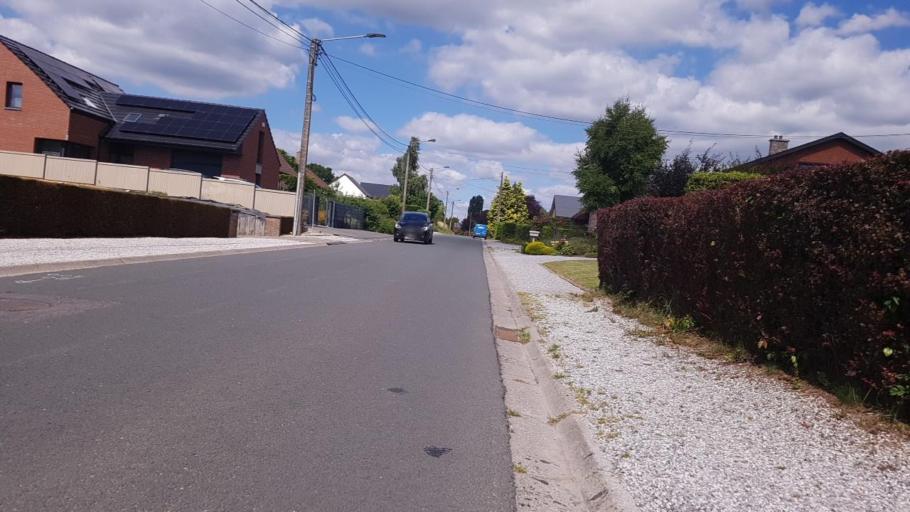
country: BE
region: Wallonia
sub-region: Province de Namur
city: Walcourt
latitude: 50.3342
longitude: 4.3889
